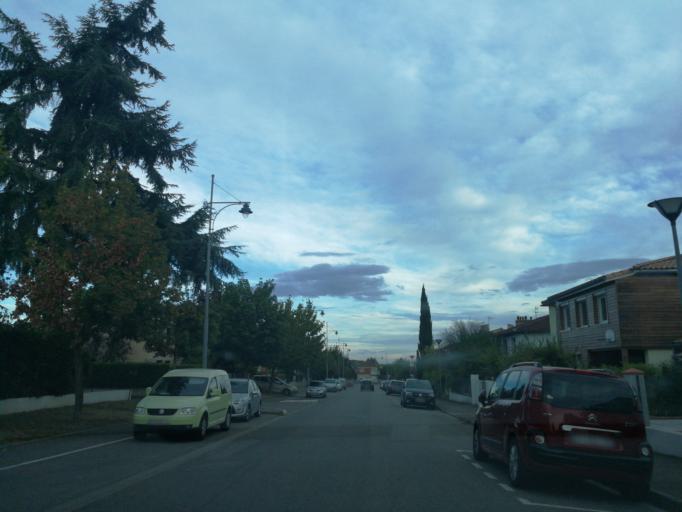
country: FR
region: Midi-Pyrenees
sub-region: Departement de la Haute-Garonne
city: L'Union
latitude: 43.6543
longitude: 1.4830
